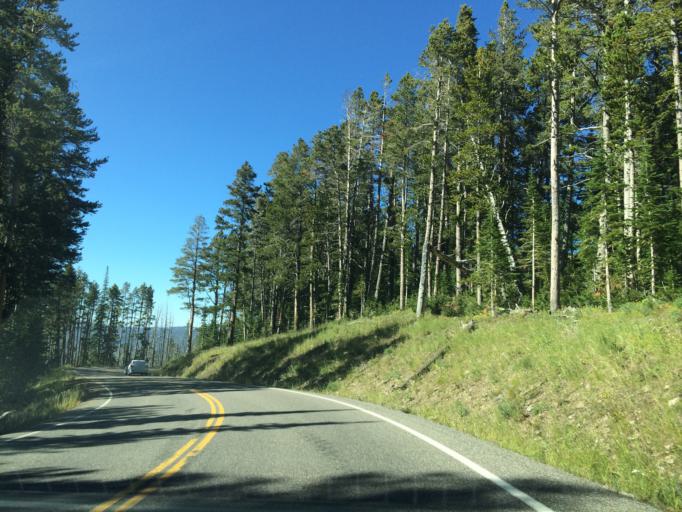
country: US
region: Montana
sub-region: Gallatin County
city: West Yellowstone
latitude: 44.8092
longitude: -110.4429
